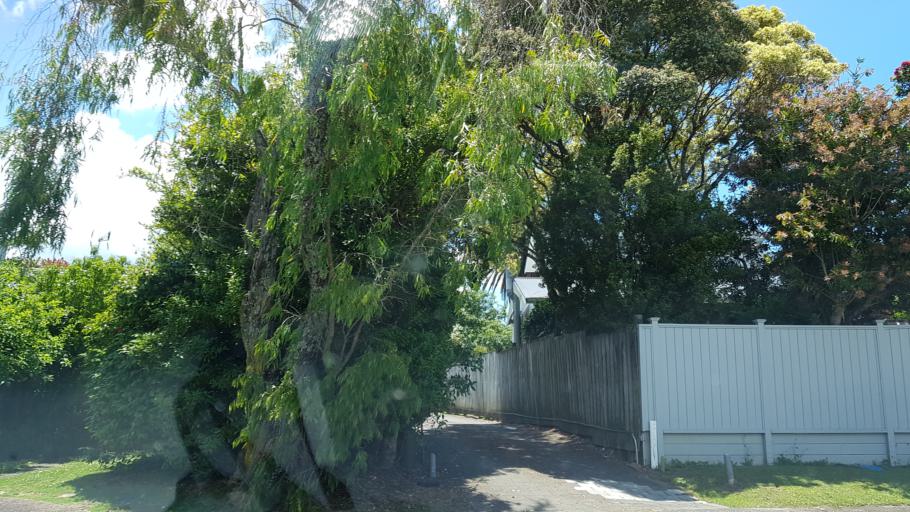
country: NZ
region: Auckland
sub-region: Auckland
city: North Shore
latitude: -36.7851
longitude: 174.6908
